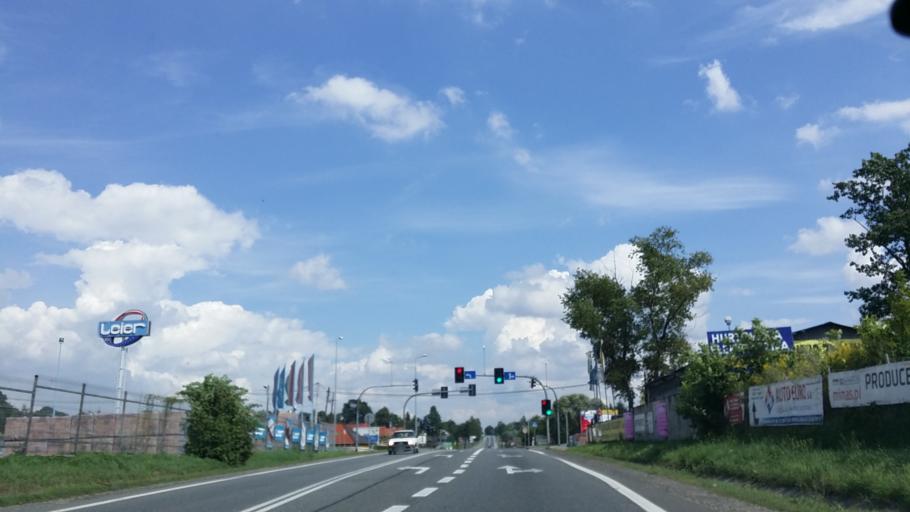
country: PL
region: Lesser Poland Voivodeship
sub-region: Powiat wielicki
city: Wieliczka
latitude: 49.9945
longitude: 20.0461
